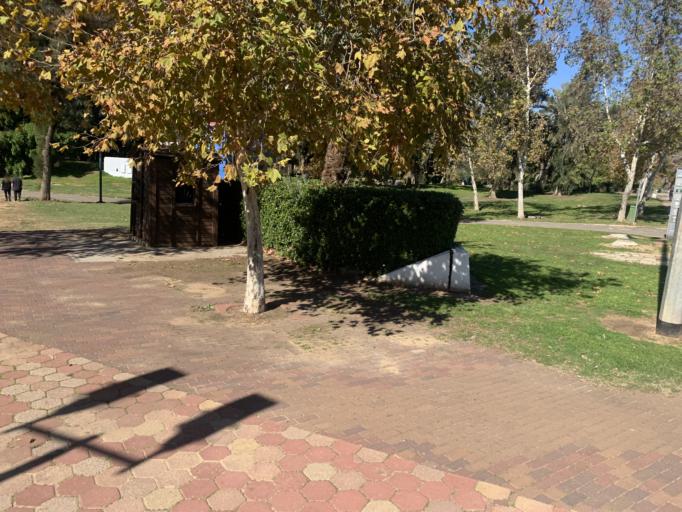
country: IL
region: Tel Aviv
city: Ramat Gan
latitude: 32.0995
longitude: 34.8091
